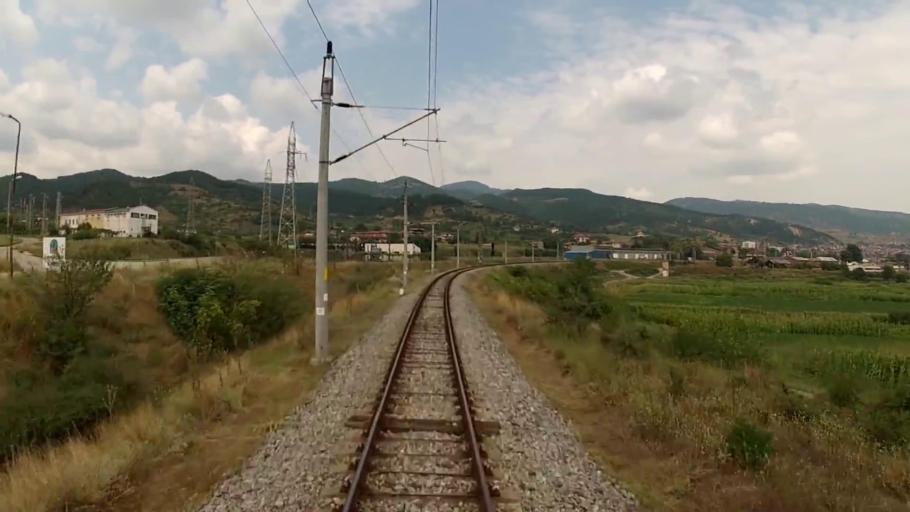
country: BG
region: Blagoevgrad
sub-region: Obshtina Simitli
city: Simitli
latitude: 41.8730
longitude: 23.1162
